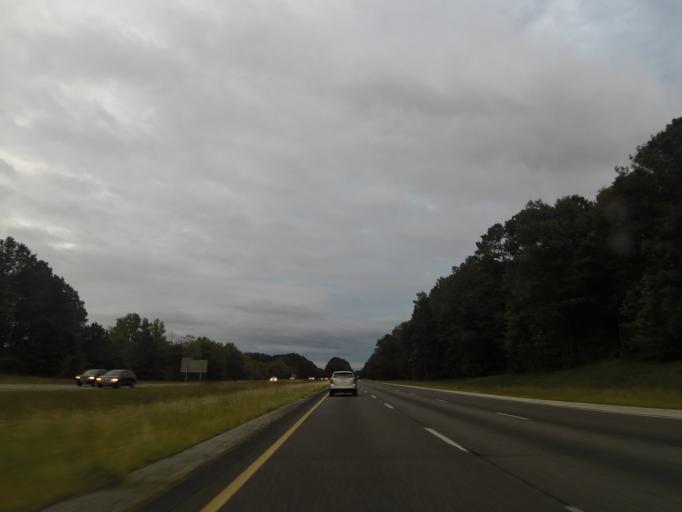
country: US
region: Alabama
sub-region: Saint Clair County
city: Springville
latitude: 33.7780
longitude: -86.4240
